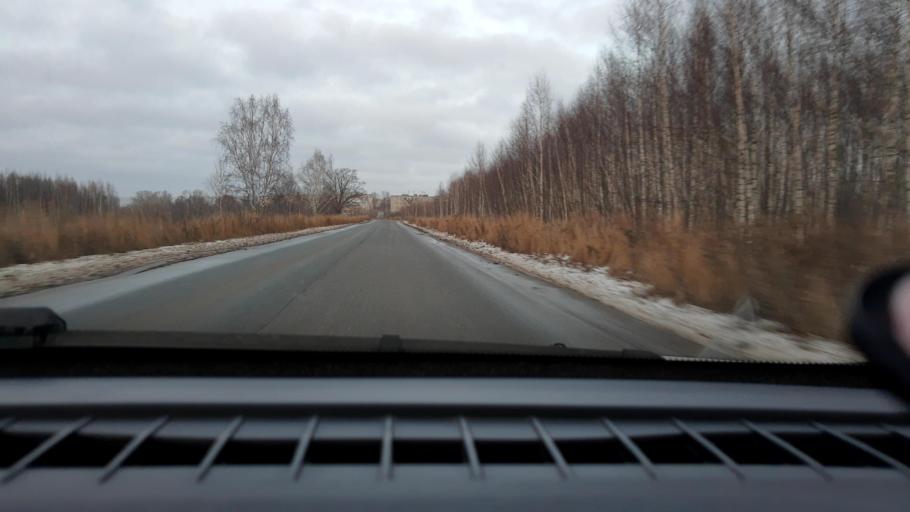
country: RU
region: Nizjnij Novgorod
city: Gorbatovka
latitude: 56.2401
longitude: 43.7431
